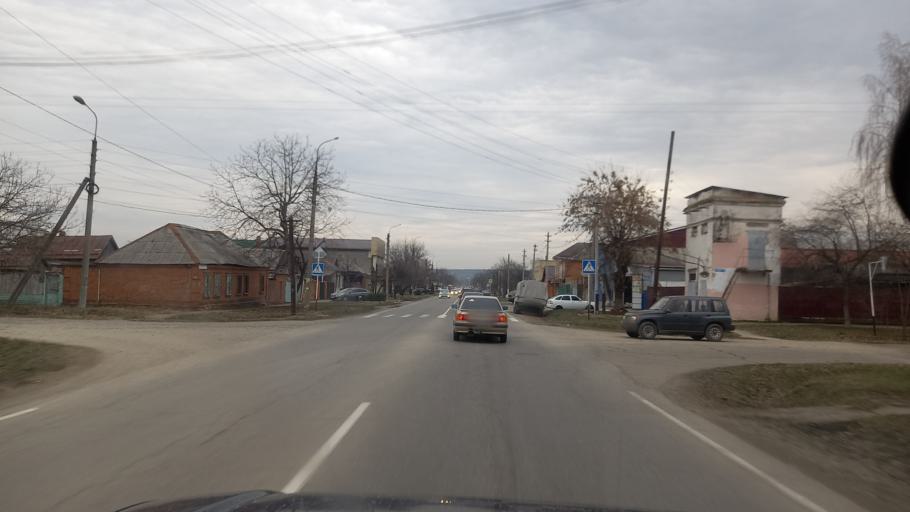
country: RU
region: Adygeya
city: Maykop
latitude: 44.5995
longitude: 40.1190
